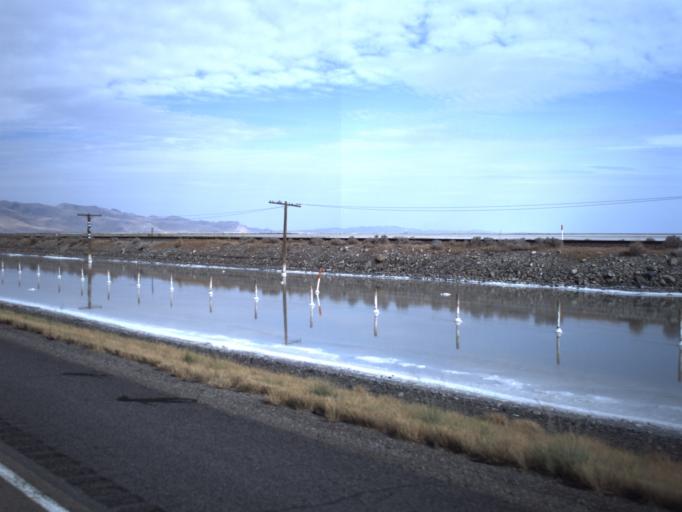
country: US
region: Utah
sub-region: Tooele County
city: Grantsville
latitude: 40.7366
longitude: -112.6097
